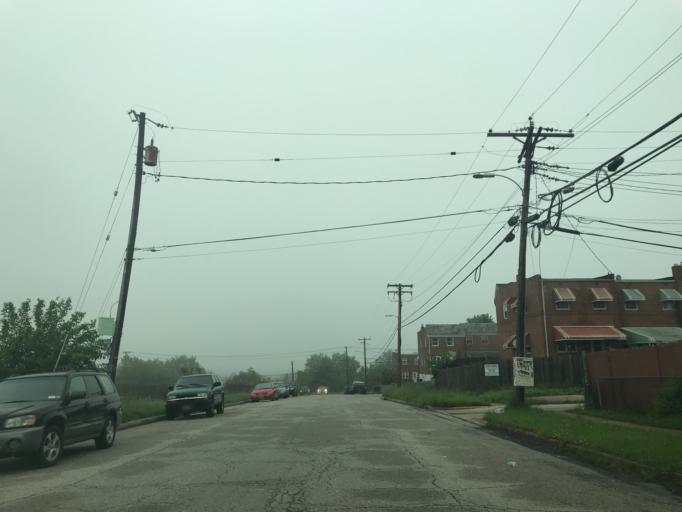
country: US
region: Maryland
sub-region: Baltimore County
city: Rosedale
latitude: 39.2958
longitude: -76.5198
